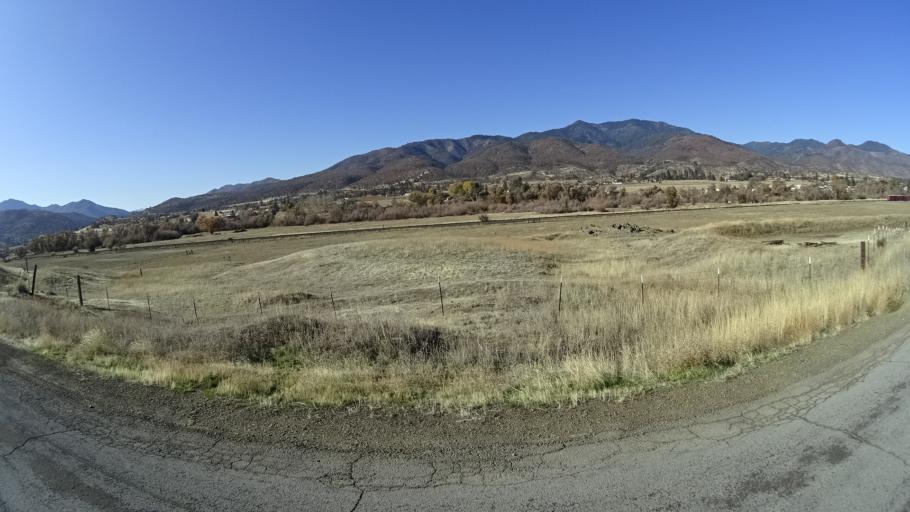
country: US
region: California
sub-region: Siskiyou County
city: Montague
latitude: 41.9043
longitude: -122.5473
